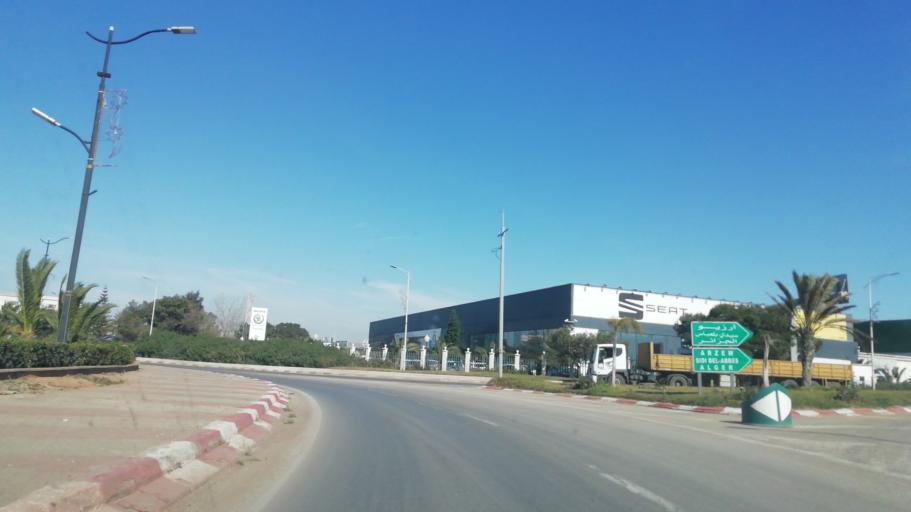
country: DZ
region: Oran
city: Es Senia
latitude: 35.6228
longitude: -0.5918
